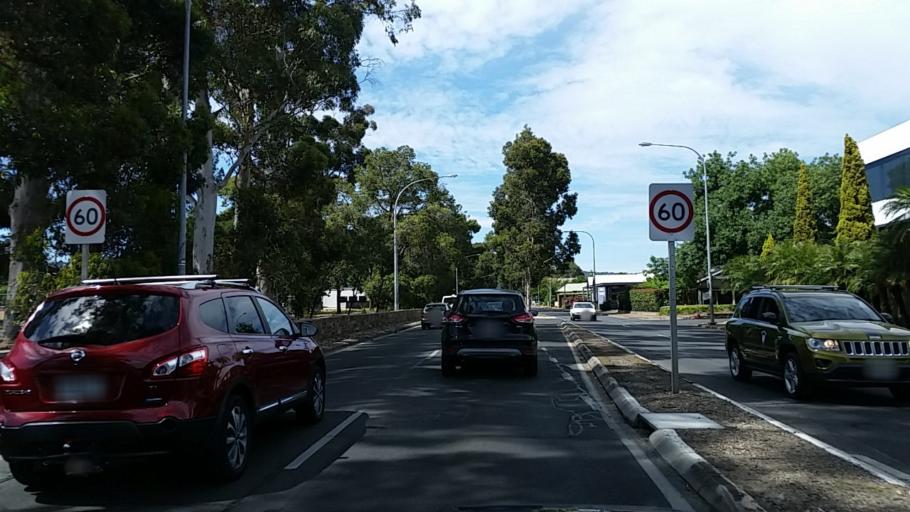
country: AU
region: South Australia
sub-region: Unley
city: Fullarton
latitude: -34.9410
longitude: 138.6247
